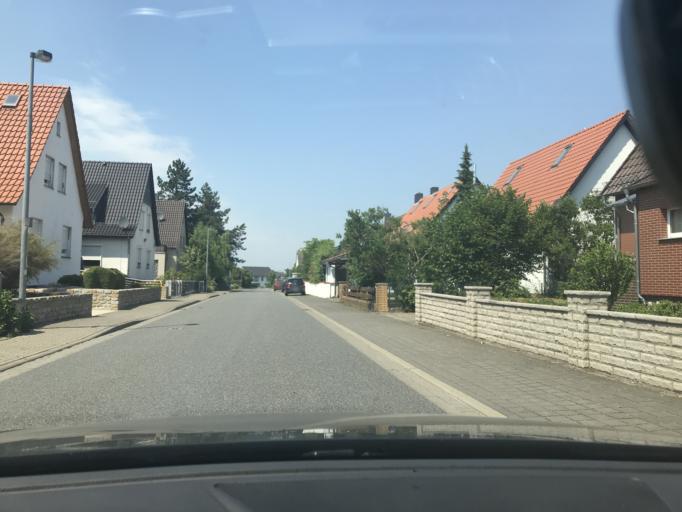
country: DE
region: Lower Saxony
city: Sehnde
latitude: 52.3477
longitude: 9.9404
